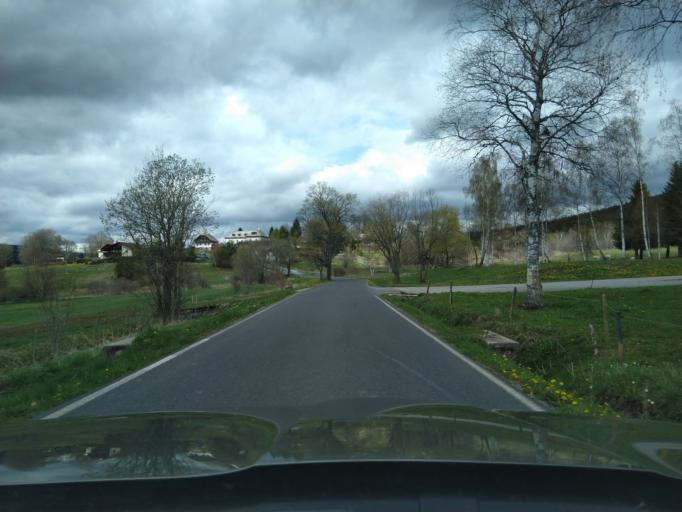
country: CZ
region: Jihocesky
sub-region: Okres Prachatice
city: Borova Lada
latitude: 49.0044
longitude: 13.6717
